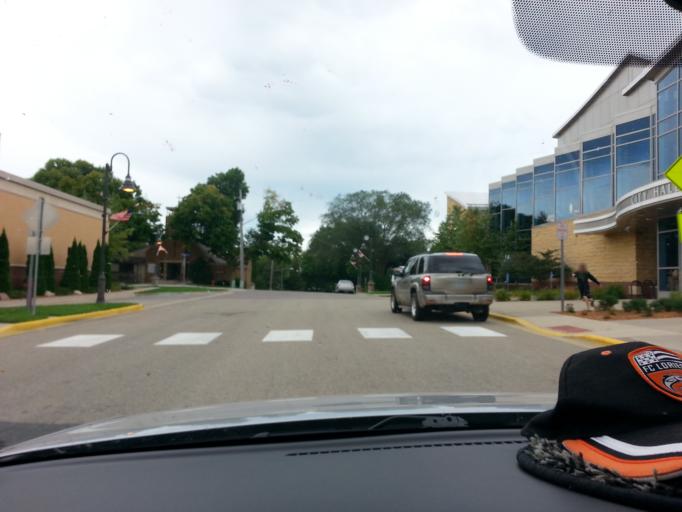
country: US
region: Minnesota
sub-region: Scott County
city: Prior Lake
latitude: 44.7152
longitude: -93.4260
